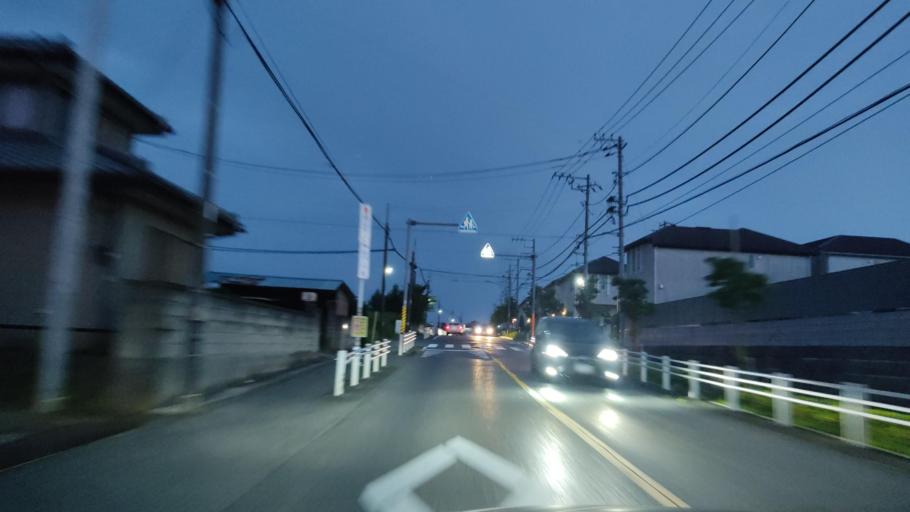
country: JP
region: Chiba
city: Nagareyama
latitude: 35.8572
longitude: 139.9115
